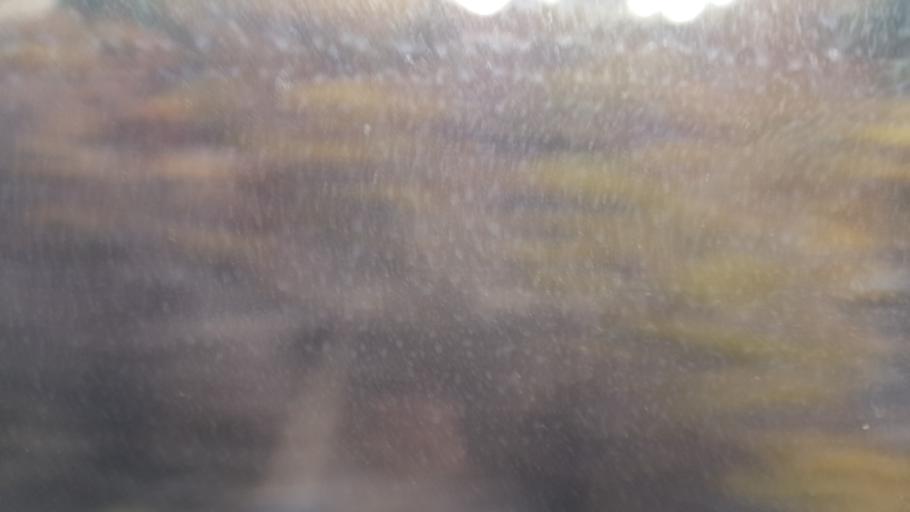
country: TR
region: Ankara
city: Nallihan
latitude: 40.0515
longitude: 31.3993
